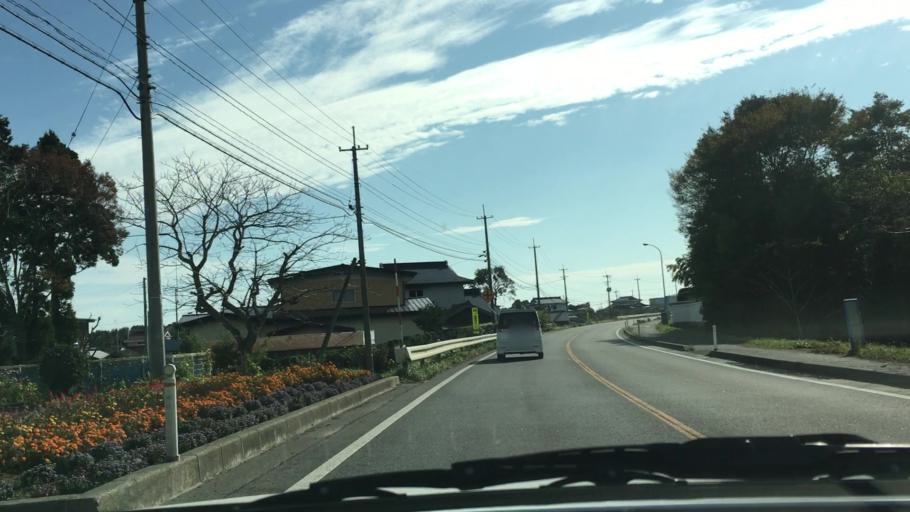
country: JP
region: Aomori
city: Hachinohe
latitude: 40.4257
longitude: 141.6964
